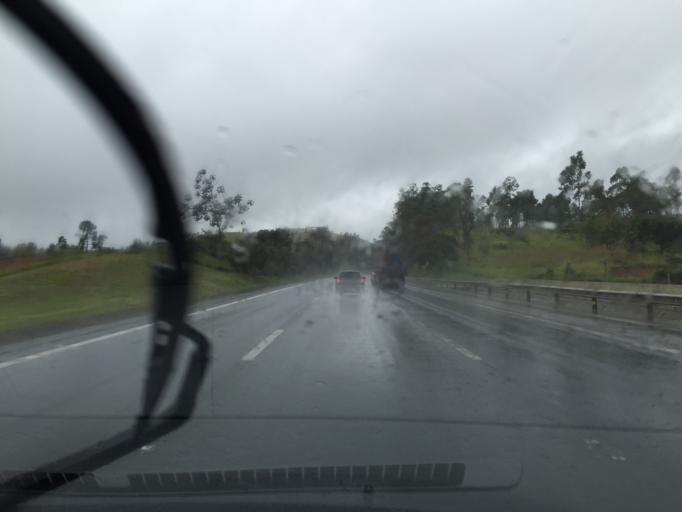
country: BR
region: Sao Paulo
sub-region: Mairinque
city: Mairinque
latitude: -23.4148
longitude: -47.2641
